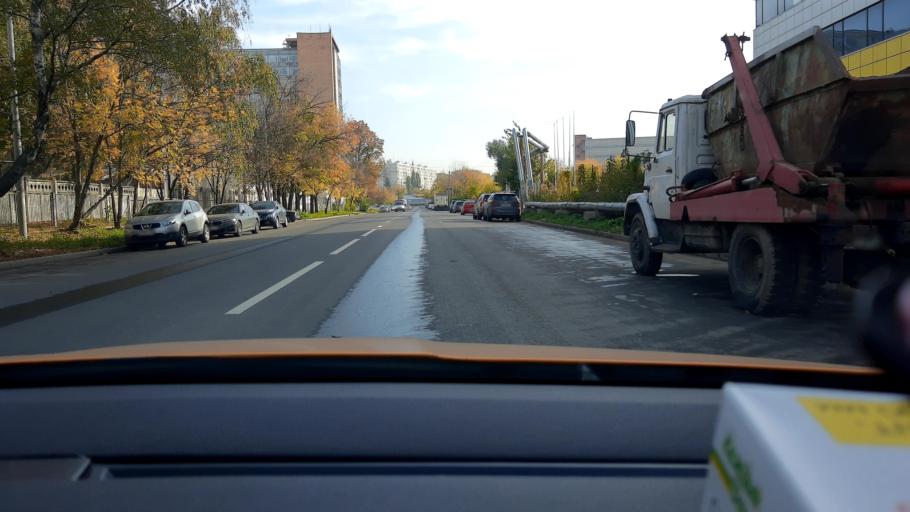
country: RU
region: Moscow
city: Slobodka
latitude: 55.8698
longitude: 37.5772
